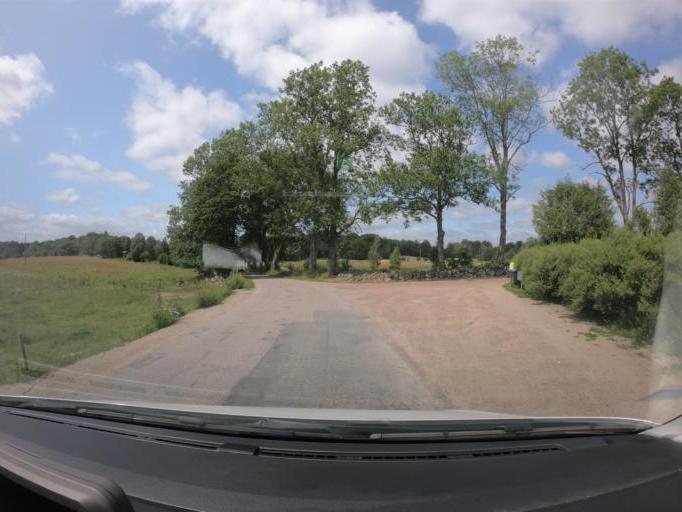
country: SE
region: Skane
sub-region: Hassleholms Kommun
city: Sosdala
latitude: 55.9869
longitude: 13.6363
